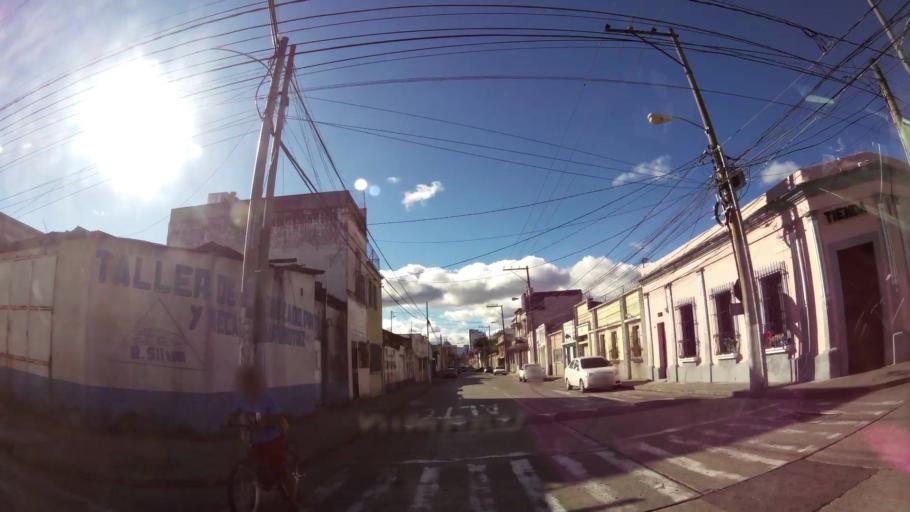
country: GT
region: Guatemala
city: Guatemala City
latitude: 14.6348
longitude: -90.5066
